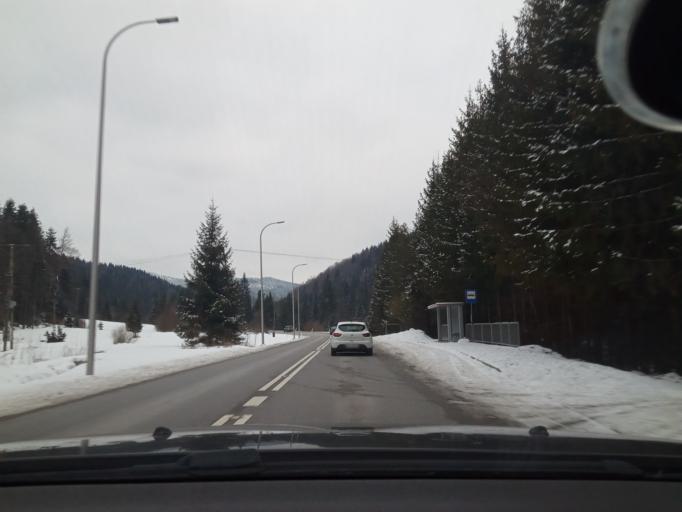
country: PL
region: Lesser Poland Voivodeship
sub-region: Powiat limanowski
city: Lubomierz
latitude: 49.6101
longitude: 20.2380
